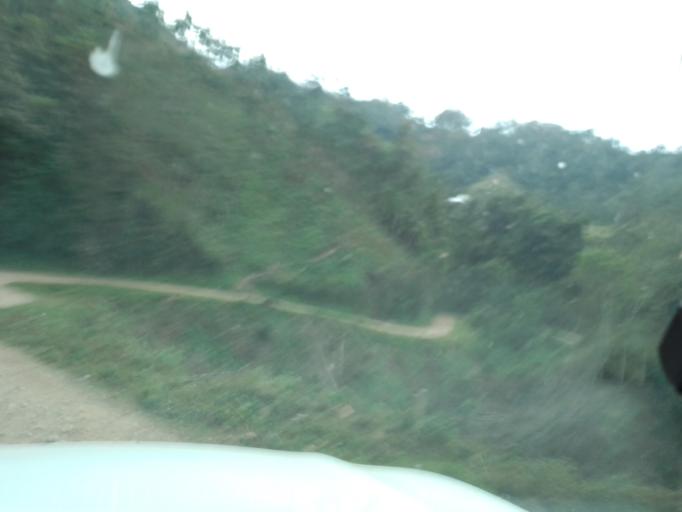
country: MX
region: Chiapas
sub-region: Cacahoatan
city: Benito Juarez
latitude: 15.2077
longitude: -92.2201
